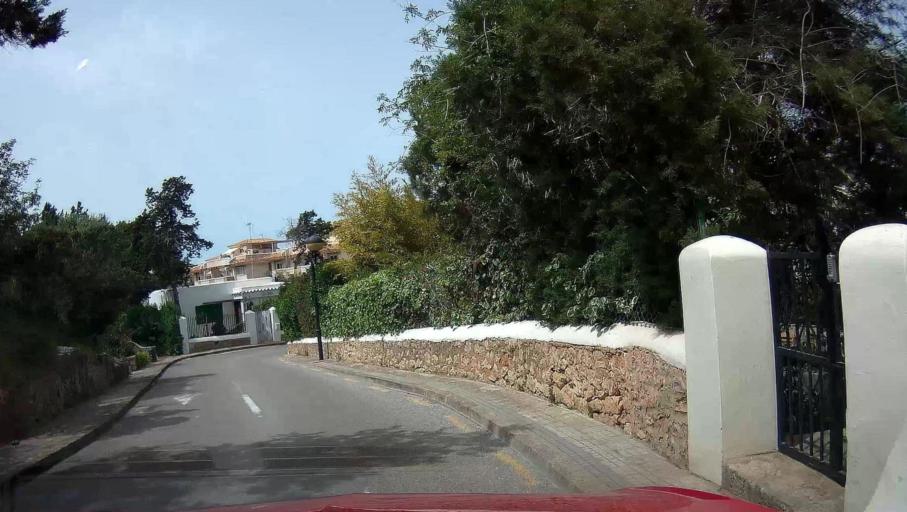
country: ES
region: Balearic Islands
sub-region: Illes Balears
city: Santa Eularia des Riu
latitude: 38.9843
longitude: 1.5304
